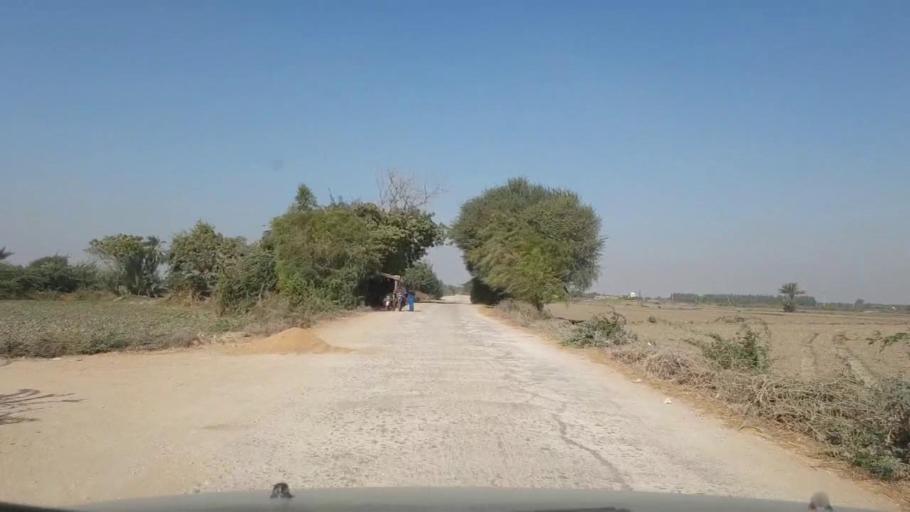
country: PK
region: Sindh
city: Thatta
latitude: 24.7878
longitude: 67.9062
